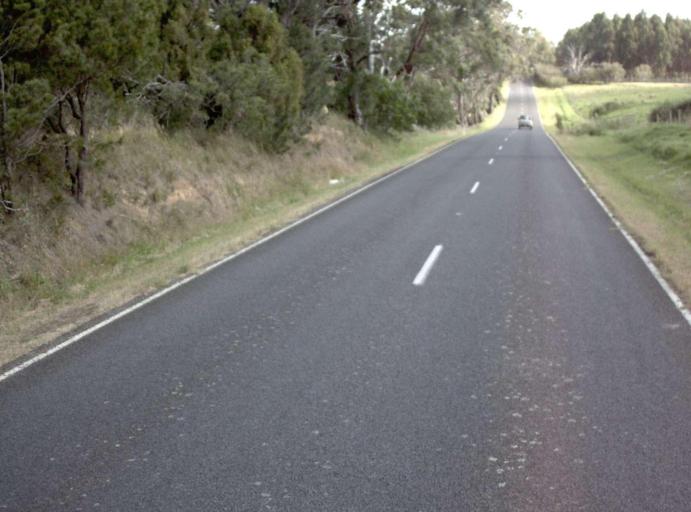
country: AU
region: Victoria
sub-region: Latrobe
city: Morwell
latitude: -38.2013
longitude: 146.4016
